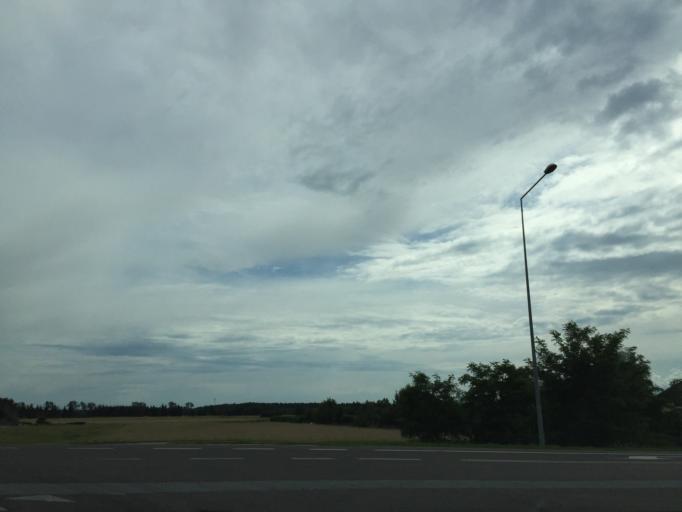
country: PL
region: Lublin Voivodeship
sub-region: Powiat bialski
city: Rzeczyca
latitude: 51.9756
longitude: 22.7415
